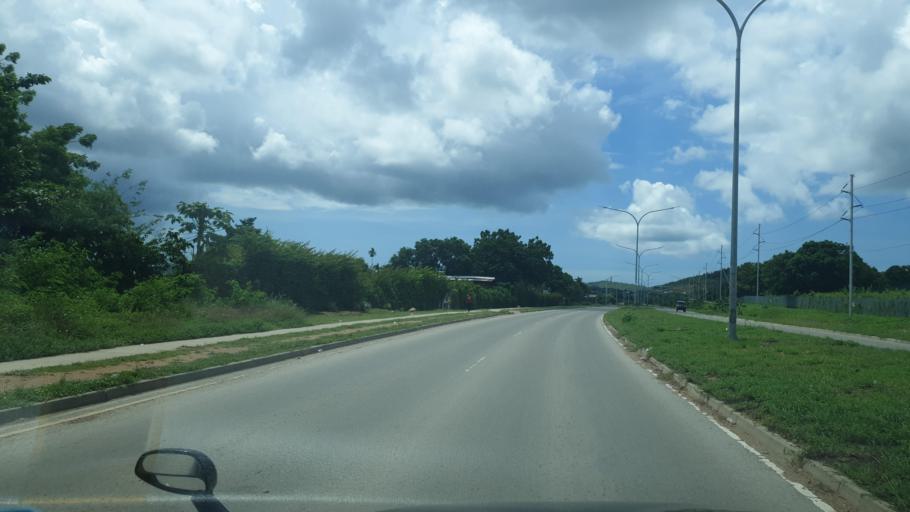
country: PG
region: National Capital
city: Port Moresby
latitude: -9.3823
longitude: 147.1557
